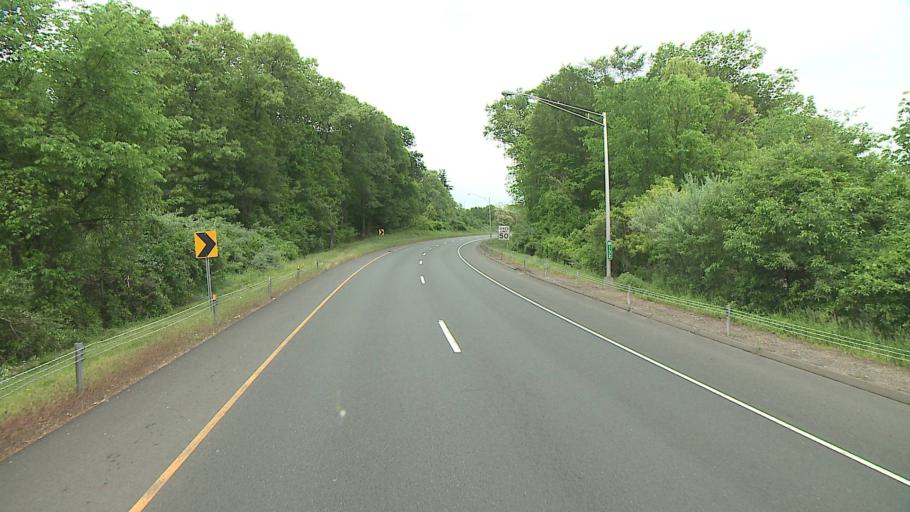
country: US
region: Connecticut
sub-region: Hartford County
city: East Hartford
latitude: 41.7718
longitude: -72.5785
